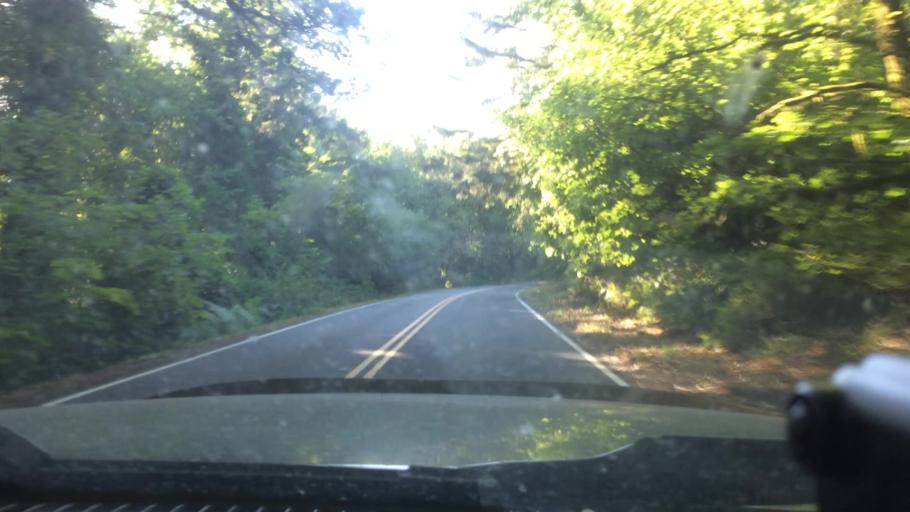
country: US
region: Oregon
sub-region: Yamhill County
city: Newberg
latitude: 45.3307
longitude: -122.9297
